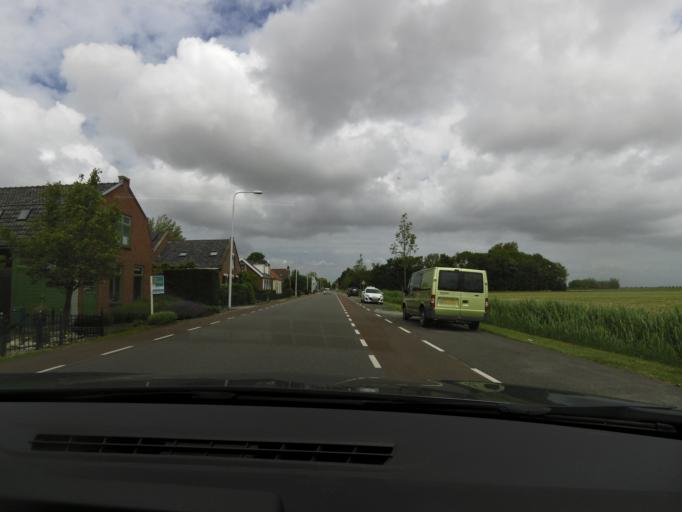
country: NL
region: South Holland
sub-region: Gemeente Goeree-Overflakkee
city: Ouddorp
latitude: 51.7073
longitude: 3.9483
